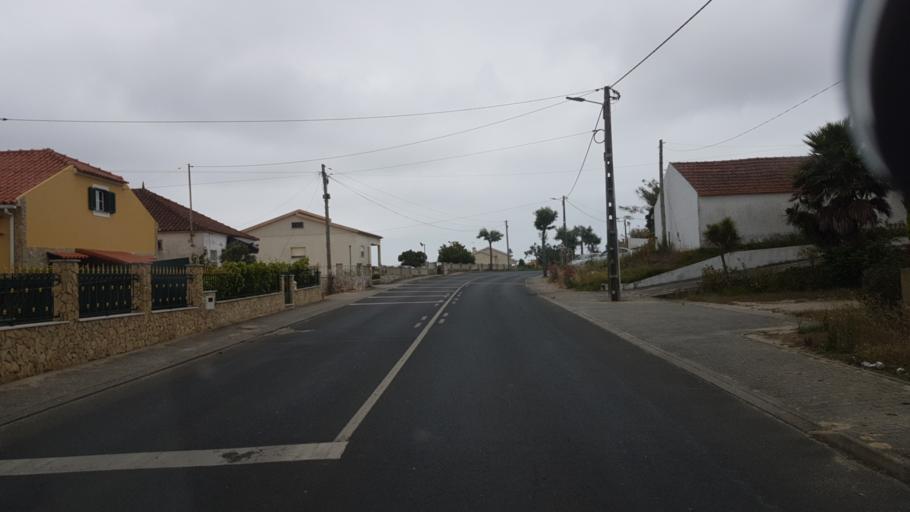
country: PT
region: Lisbon
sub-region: Lourinha
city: Lourinha
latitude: 39.2105
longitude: -9.3189
